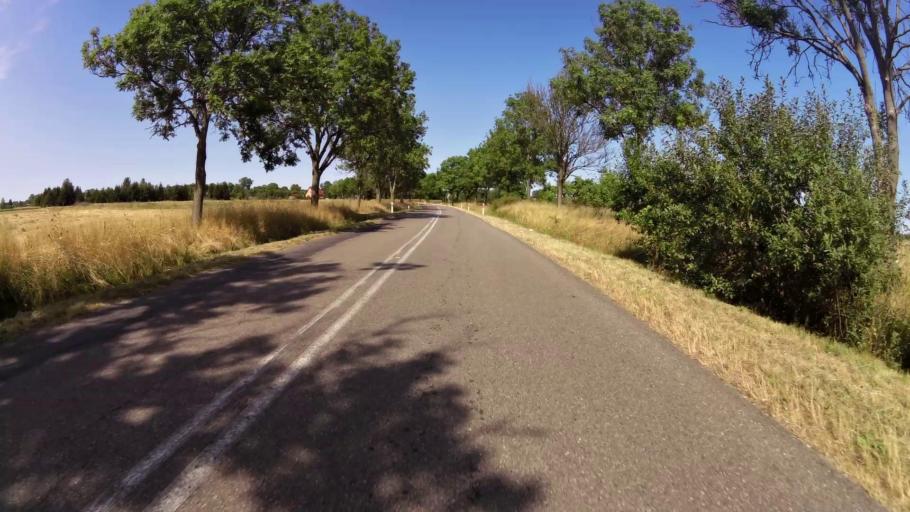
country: PL
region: West Pomeranian Voivodeship
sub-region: Powiat stargardzki
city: Suchan
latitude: 53.3021
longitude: 15.3692
